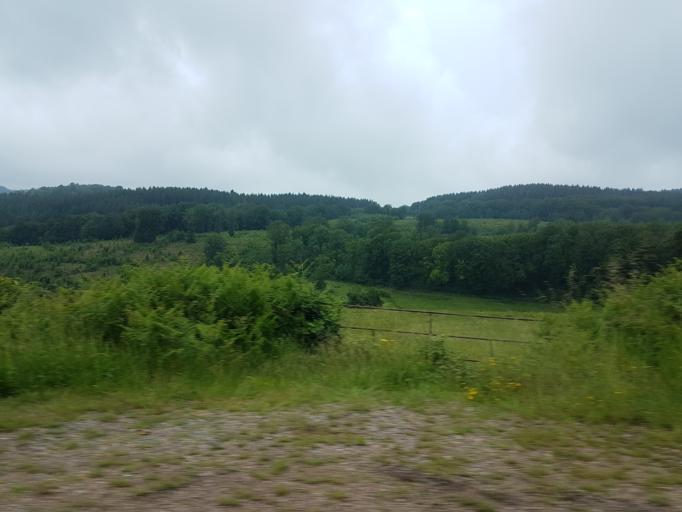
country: FR
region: Bourgogne
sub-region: Departement de la Nievre
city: Chateau-Chinon(Ville)
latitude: 47.0518
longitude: 3.9385
